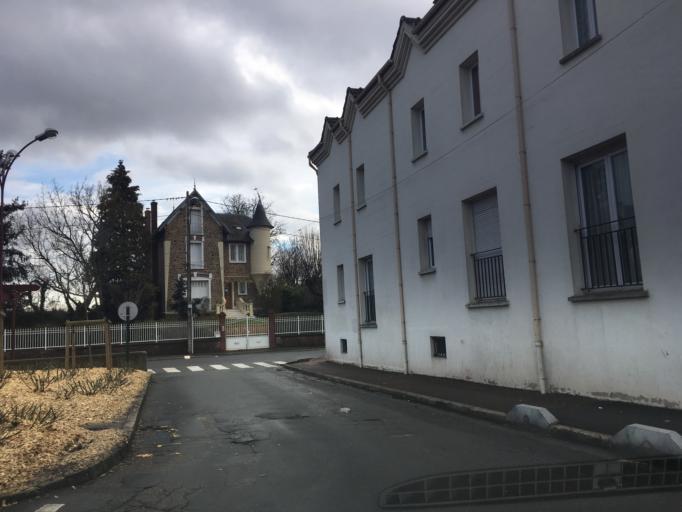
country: FR
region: Ile-de-France
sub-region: Departement du Val-d'Oise
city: Arnouville
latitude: 48.9978
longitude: 2.4205
